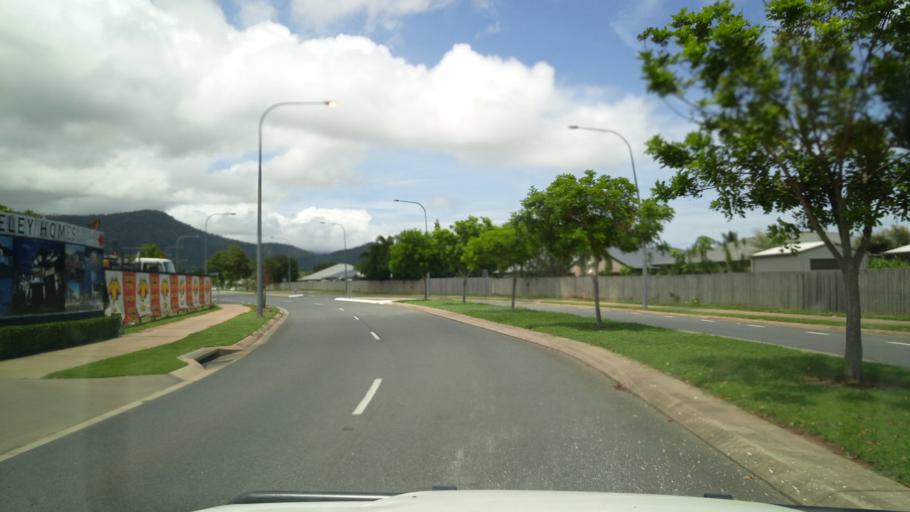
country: AU
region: Queensland
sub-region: Cairns
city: Yorkeys Knob
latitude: -16.8343
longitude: 145.6963
